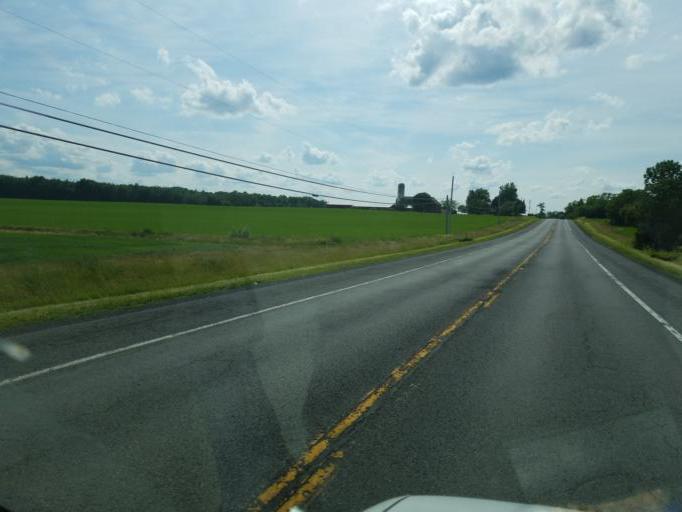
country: US
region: New York
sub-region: Ontario County
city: Shortsville
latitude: 42.8617
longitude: -77.1796
